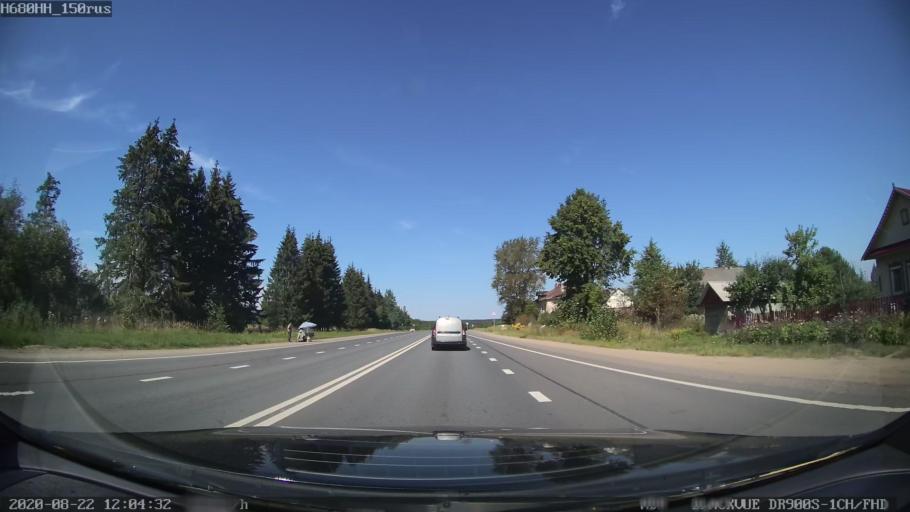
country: RU
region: Tverskaya
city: Rameshki
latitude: 57.2685
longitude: 36.0727
